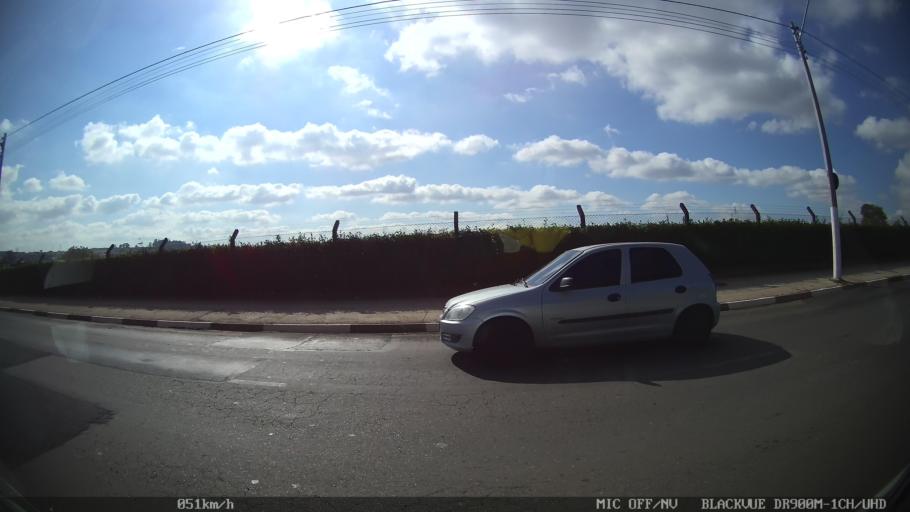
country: BR
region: Sao Paulo
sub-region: Hortolandia
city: Hortolandia
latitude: -22.8748
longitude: -47.1997
